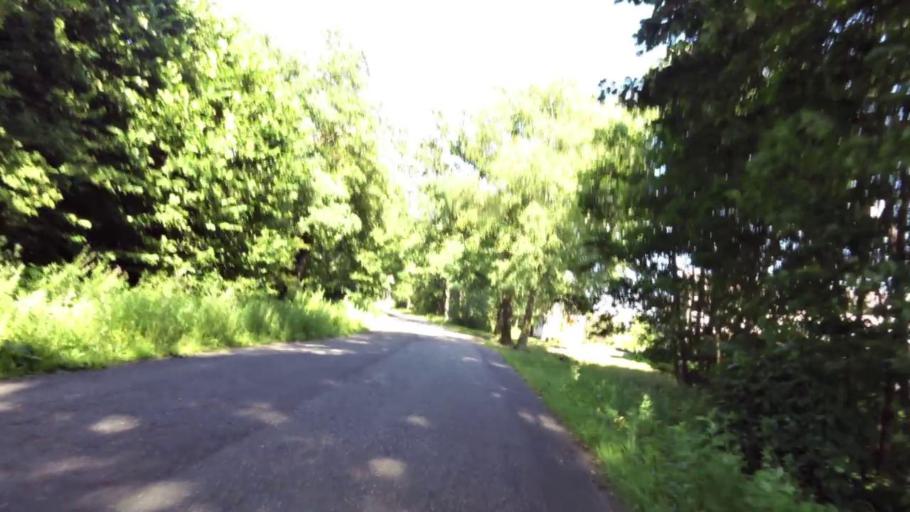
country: PL
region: West Pomeranian Voivodeship
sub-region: Powiat slawienski
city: Slawno
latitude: 54.4366
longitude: 16.7530
